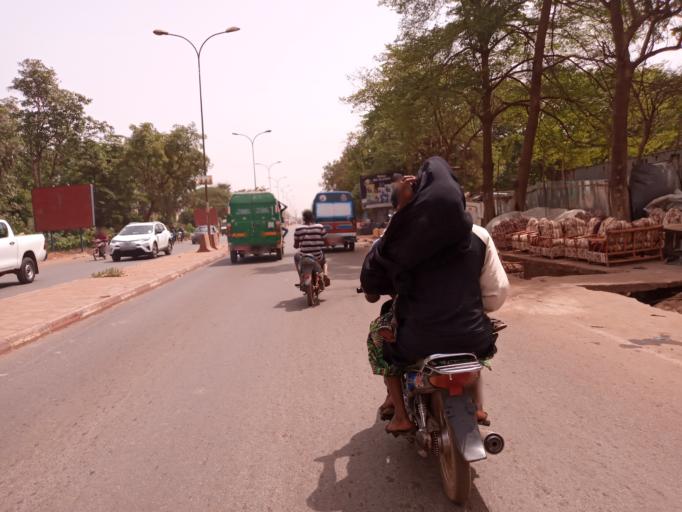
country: ML
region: Bamako
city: Bamako
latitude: 12.6566
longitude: -7.9703
